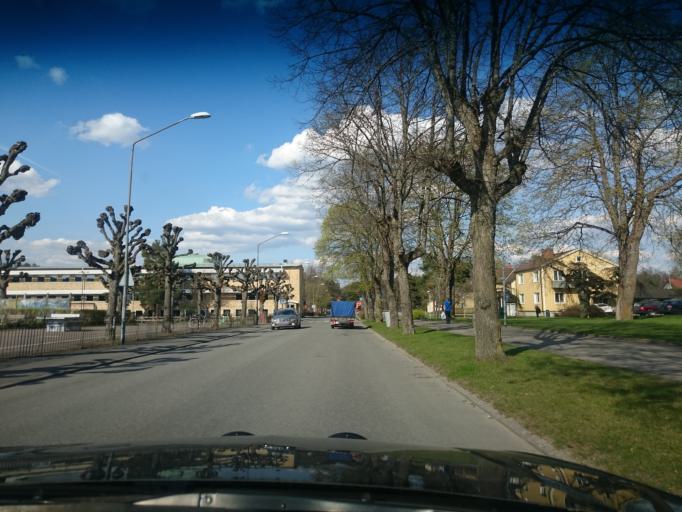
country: SE
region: Joenkoeping
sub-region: Vetlanda Kommun
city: Vetlanda
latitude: 57.4288
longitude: 15.0822
